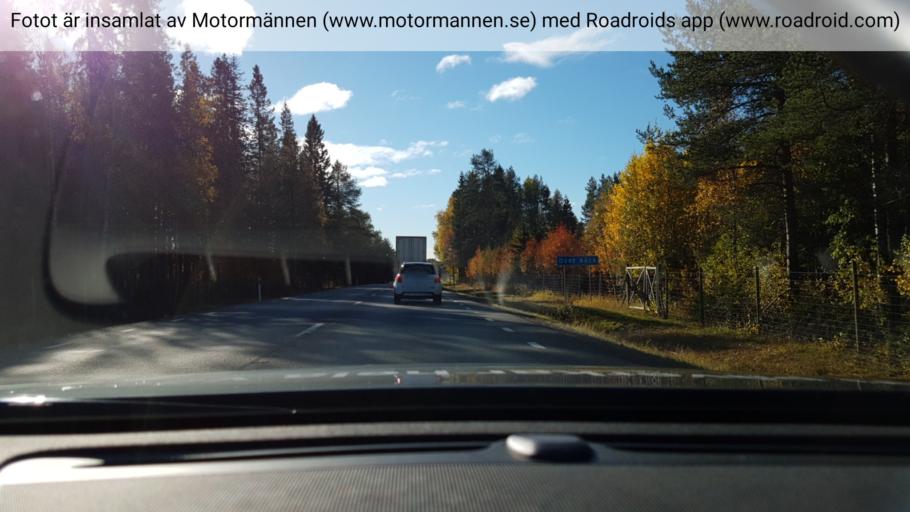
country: SE
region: Vaesterbotten
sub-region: Skelleftea Kommun
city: Burea
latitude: 64.5190
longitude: 21.2585
